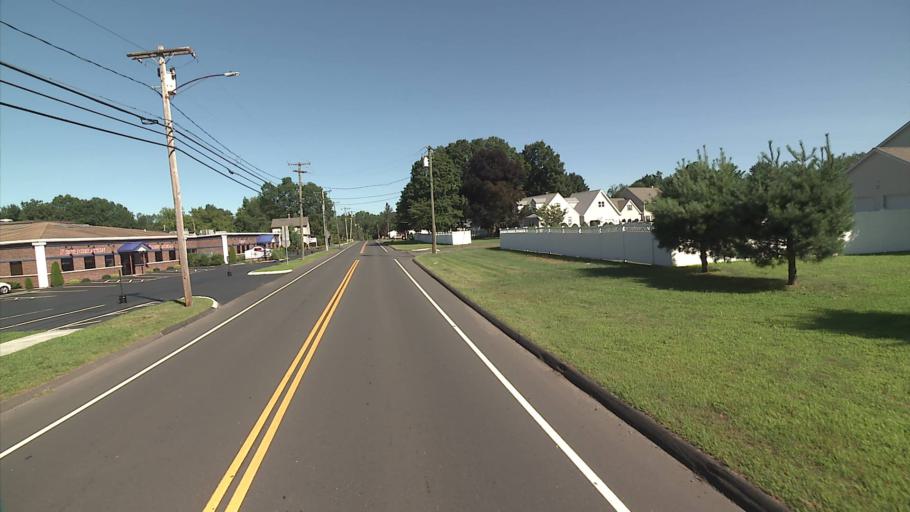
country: US
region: Connecticut
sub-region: New Haven County
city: Cheshire Village
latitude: 41.5667
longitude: -72.8929
